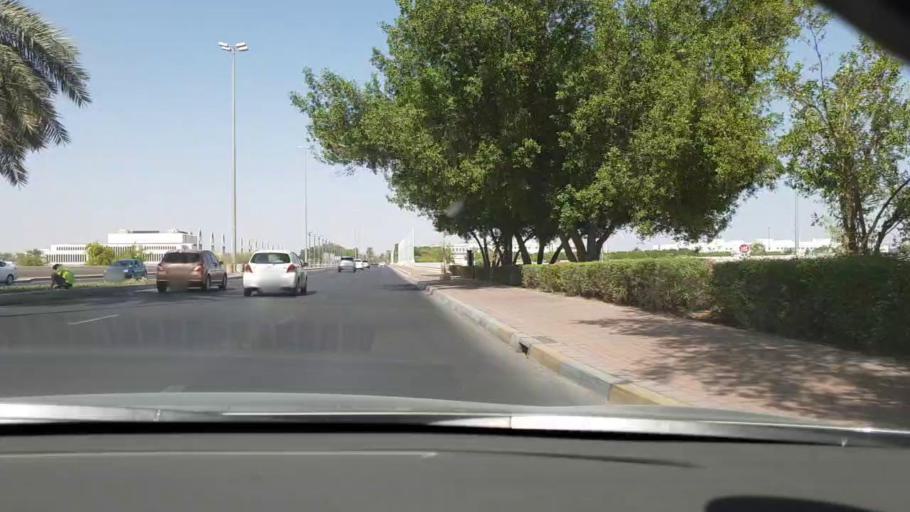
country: AE
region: Abu Dhabi
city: Al Ain
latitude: 24.2334
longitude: 55.7386
